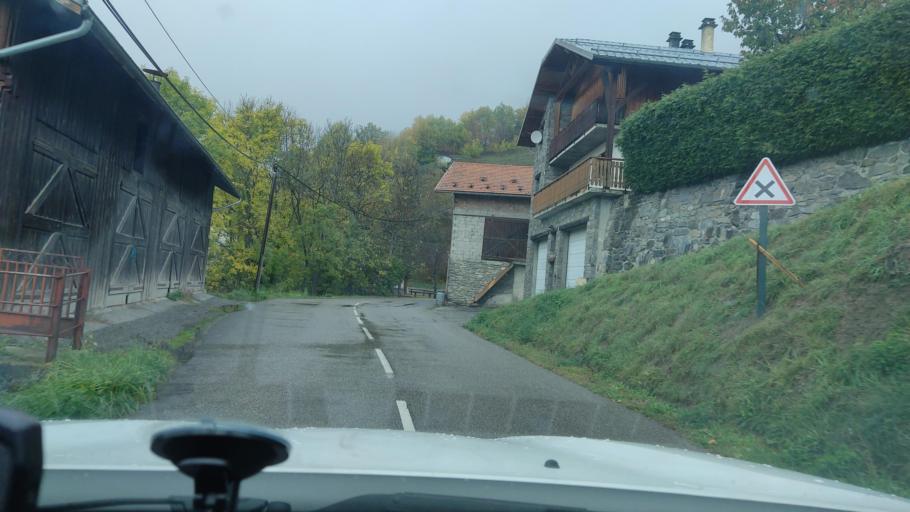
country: FR
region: Rhone-Alpes
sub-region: Departement de la Savoie
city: Les Allues
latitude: 45.4620
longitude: 6.5783
